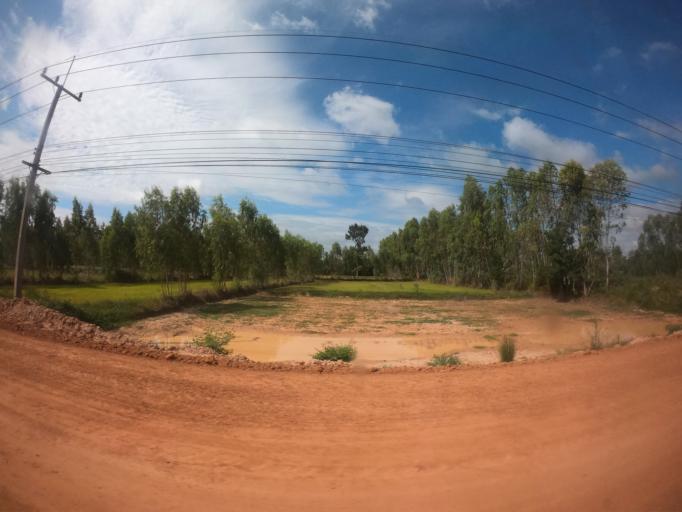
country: TH
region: Surin
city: Kap Choeng
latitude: 14.4594
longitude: 103.6638
